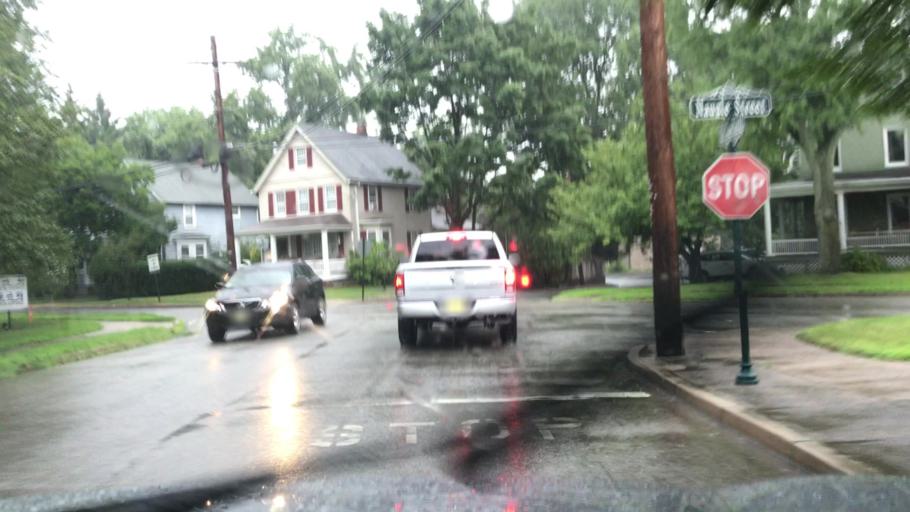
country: US
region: New Jersey
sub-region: Bergen County
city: Closter
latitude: 40.9752
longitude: -73.9625
